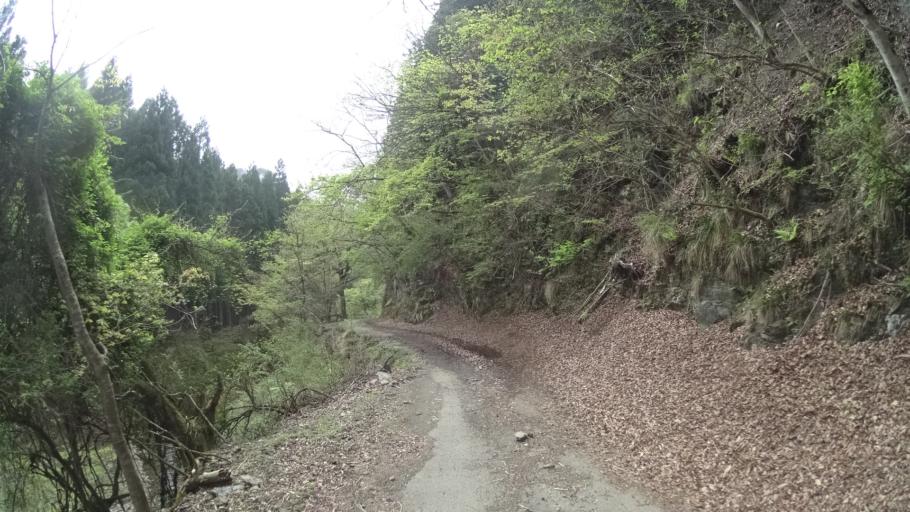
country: JP
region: Kyoto
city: Maizuru
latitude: 35.3997
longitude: 135.5017
